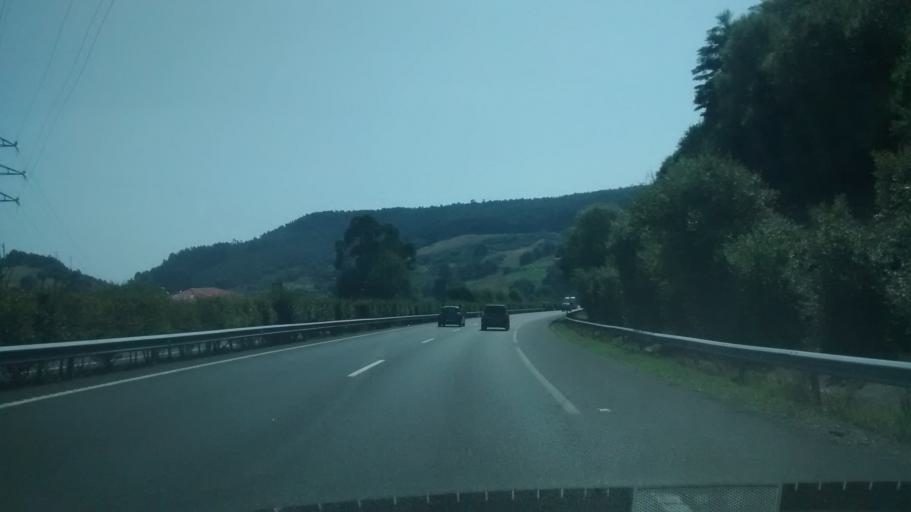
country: ES
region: Cantabria
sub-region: Provincia de Cantabria
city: Barcena de Cicero
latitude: 43.4111
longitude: -3.5184
